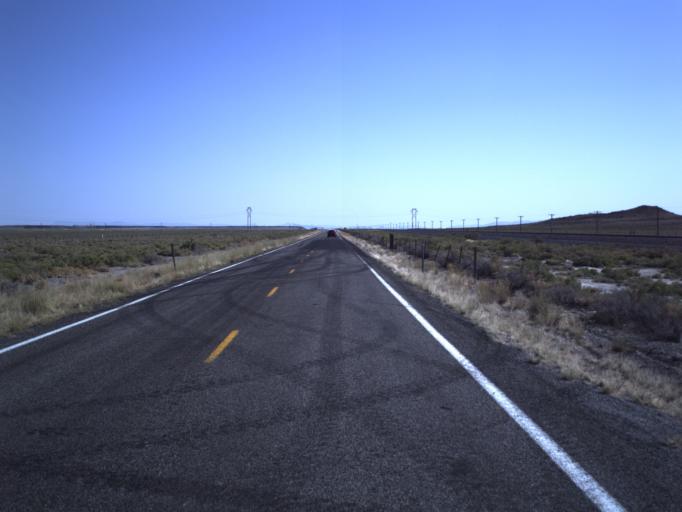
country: US
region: Utah
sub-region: Millard County
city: Delta
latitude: 39.1438
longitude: -112.7232
